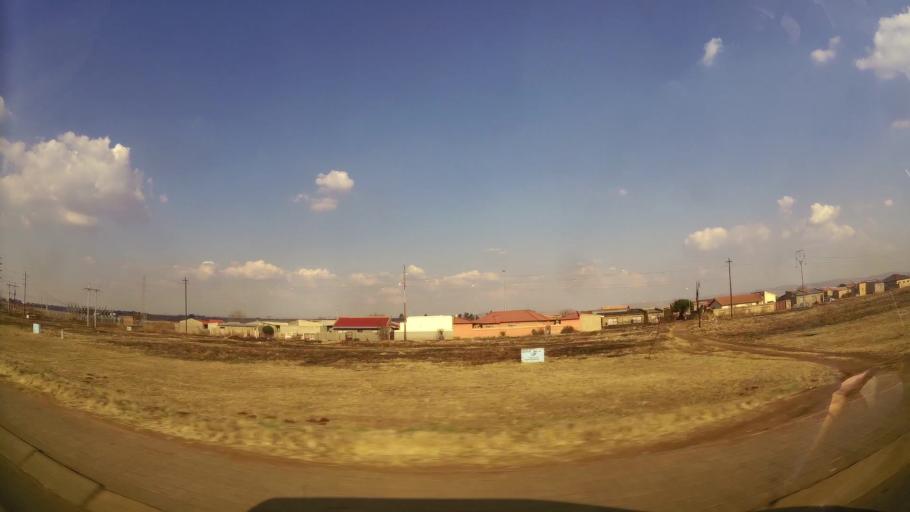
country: ZA
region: Gauteng
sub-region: Ekurhuleni Metropolitan Municipality
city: Germiston
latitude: -26.3747
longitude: 28.2127
